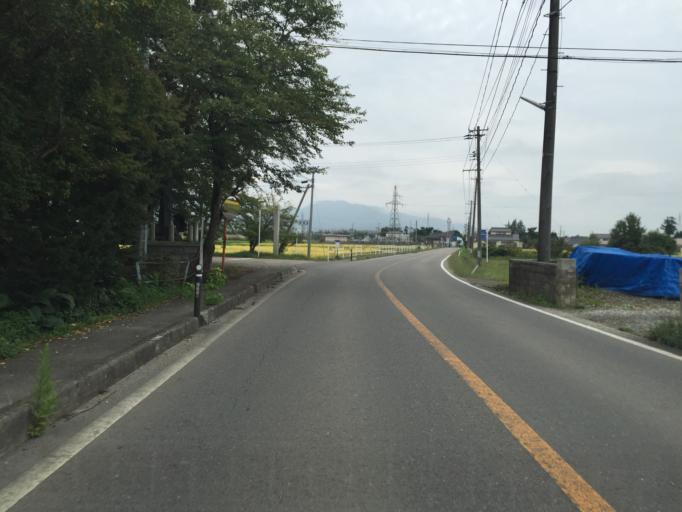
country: JP
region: Fukushima
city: Kitakata
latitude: 37.5336
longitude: 139.9312
